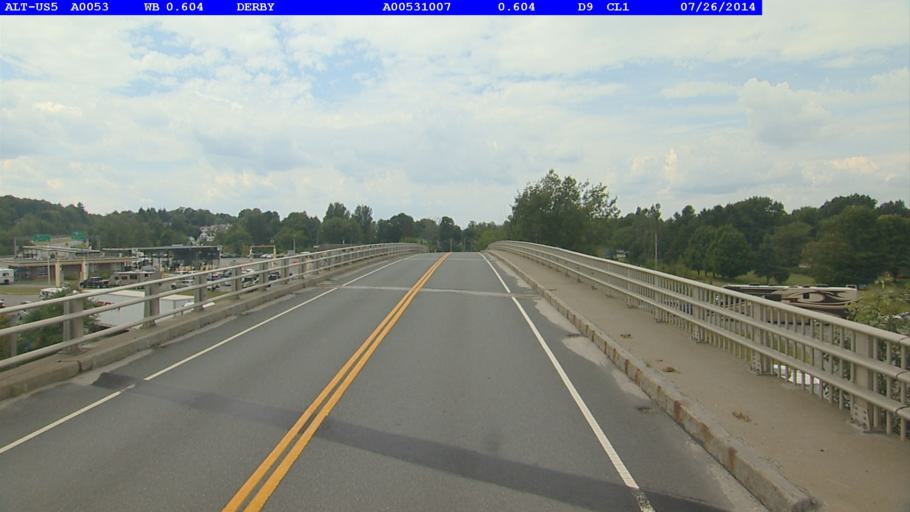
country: US
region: Vermont
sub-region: Orleans County
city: Newport
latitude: 45.0053
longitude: -72.0876
